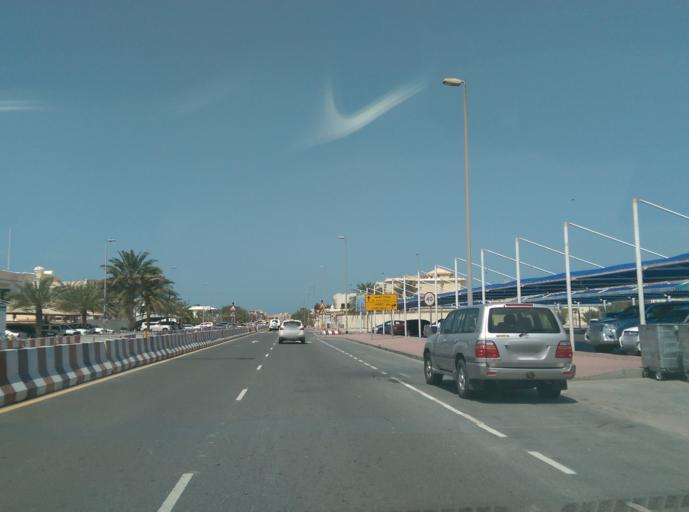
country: AE
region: Dubai
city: Dubai
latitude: 25.1865
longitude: 55.2385
